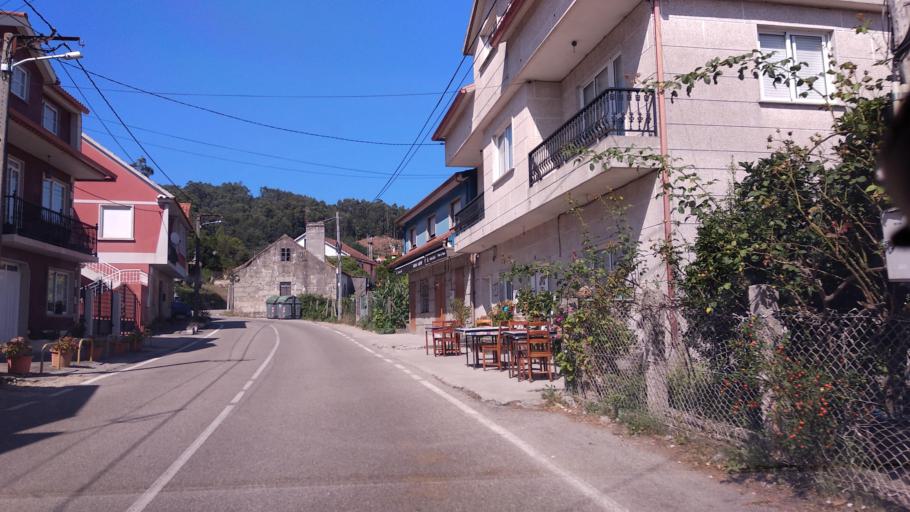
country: ES
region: Galicia
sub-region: Provincia de Pontevedra
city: Moana
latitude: 42.2770
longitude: -8.7592
